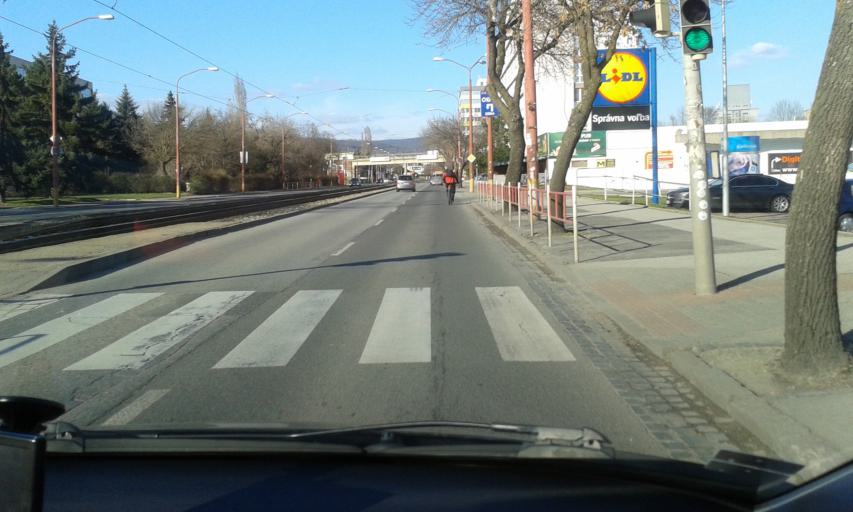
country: SK
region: Bratislavsky
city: Bratislava
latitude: 48.1779
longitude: 17.1283
